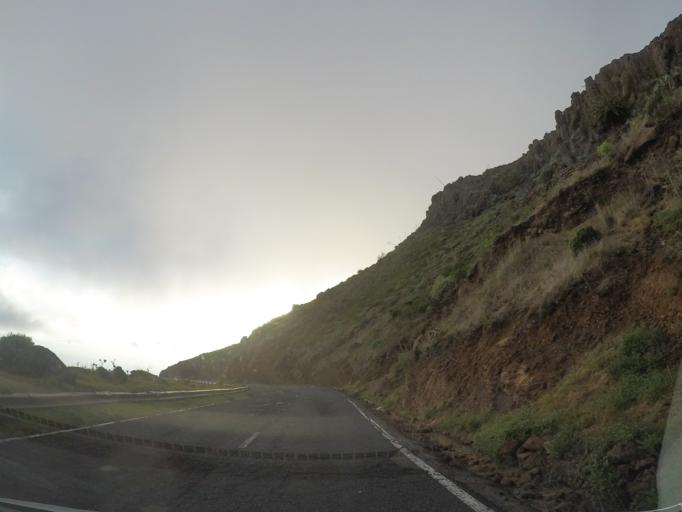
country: ES
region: Canary Islands
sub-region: Provincia de Santa Cruz de Tenerife
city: Alajero
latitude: 28.0911
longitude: -17.2527
